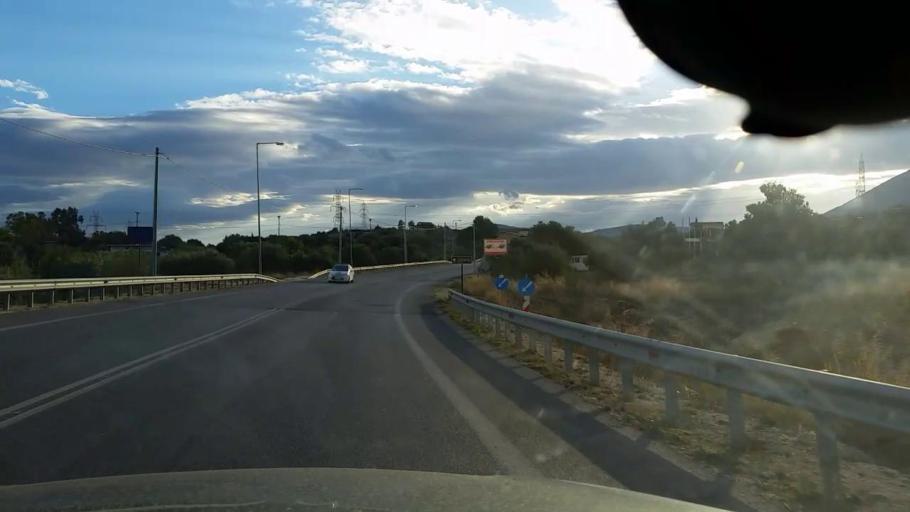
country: GR
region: Attica
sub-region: Nomarchia Anatolikis Attikis
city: Argithea
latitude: 37.9584
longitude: 23.8939
